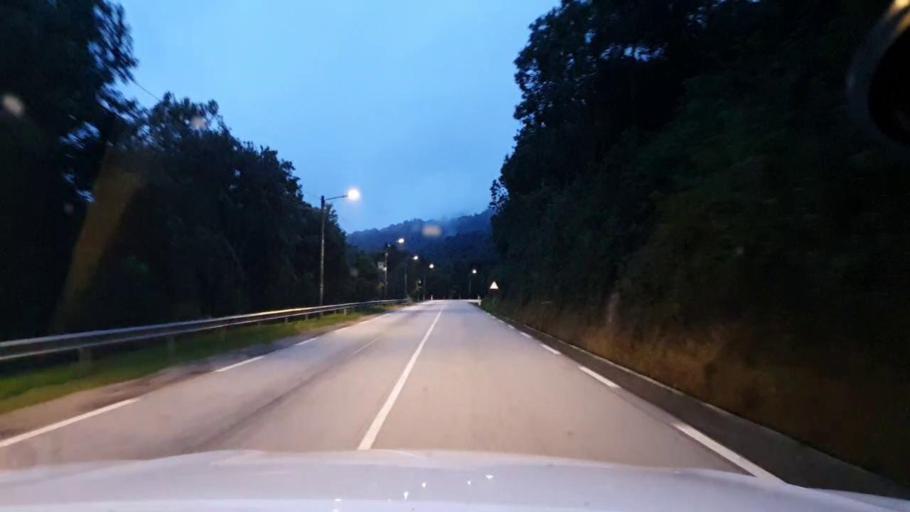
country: RW
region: Southern Province
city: Nzega
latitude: -2.5277
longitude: 29.3799
